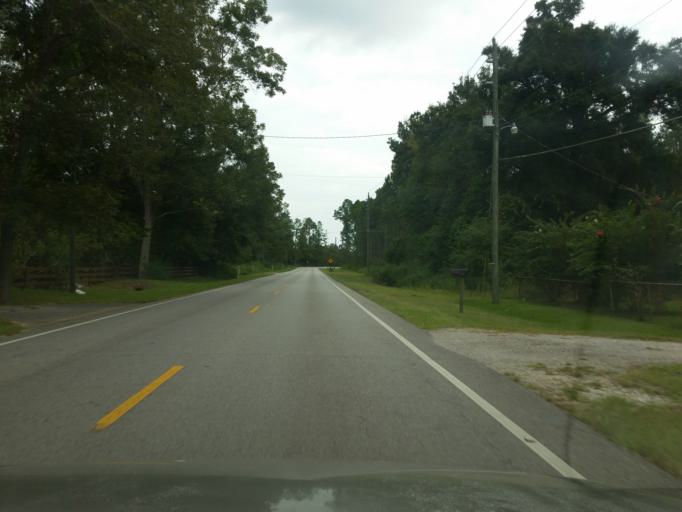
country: US
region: Florida
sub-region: Escambia County
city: Molino
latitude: 30.6806
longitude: -87.3210
